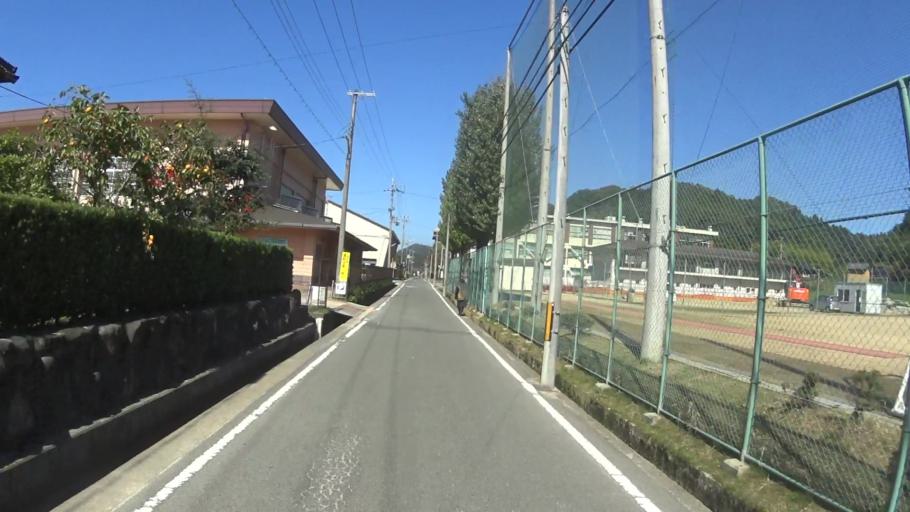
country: JP
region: Hyogo
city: Toyooka
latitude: 35.5910
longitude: 134.9318
